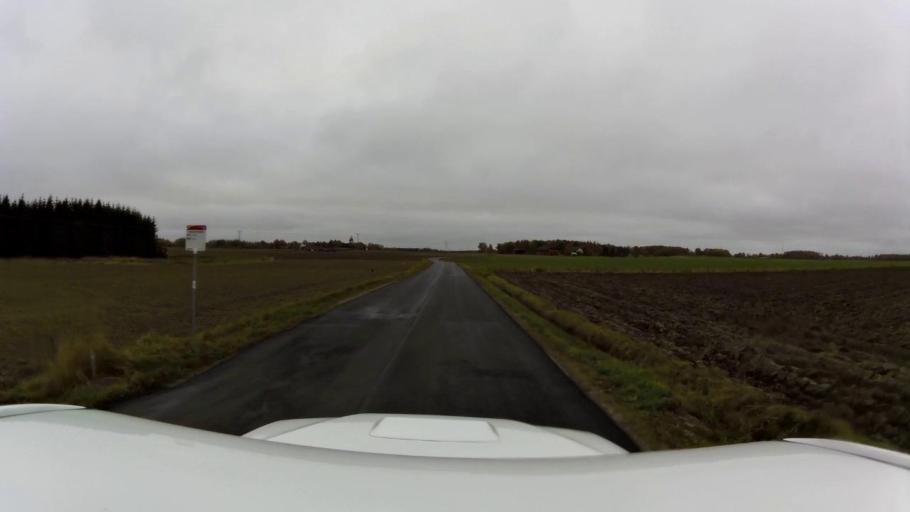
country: SE
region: OEstergoetland
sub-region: Linkopings Kommun
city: Ekangen
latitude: 58.4587
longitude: 15.7040
